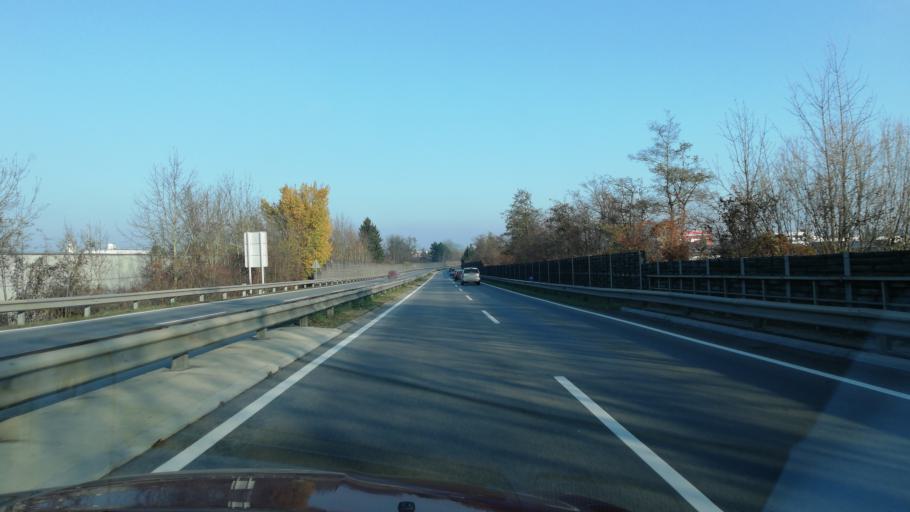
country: AT
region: Upper Austria
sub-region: Wels-Land
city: Thalheim bei Wels
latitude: 48.1526
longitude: 14.0441
